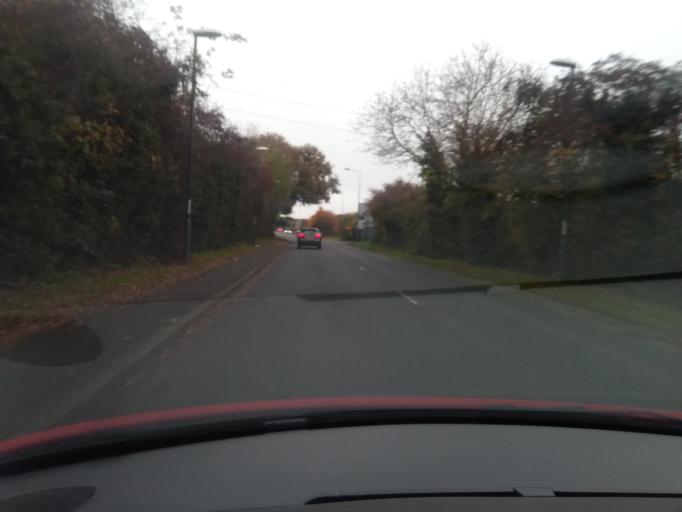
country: GB
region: England
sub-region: Derbyshire
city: Borrowash
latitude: 52.8871
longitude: -1.4114
